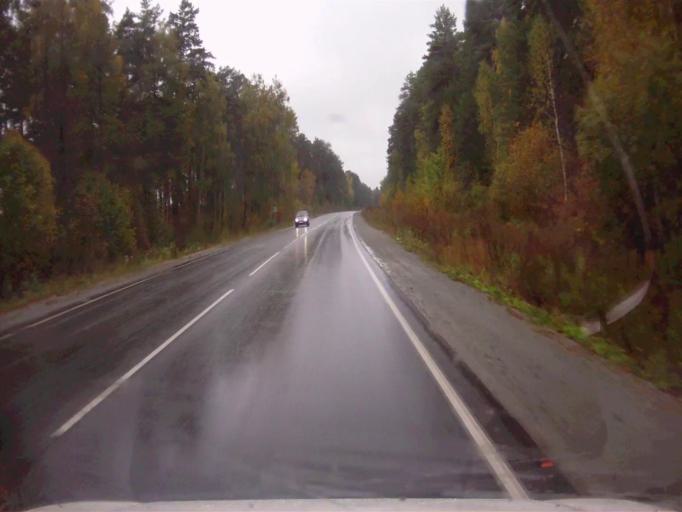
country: RU
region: Chelyabinsk
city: Kyshtym
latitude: 55.6370
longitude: 60.5953
